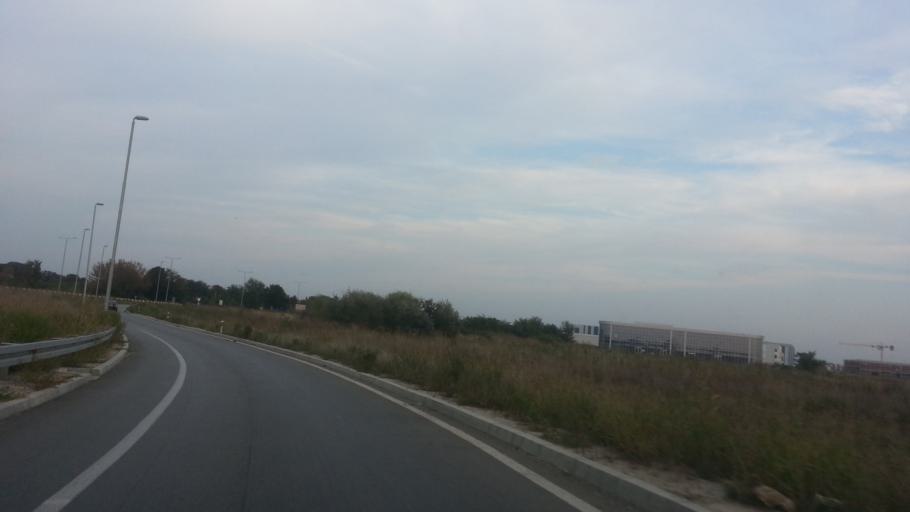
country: RS
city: Novi Banovci
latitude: 44.8868
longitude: 20.3010
